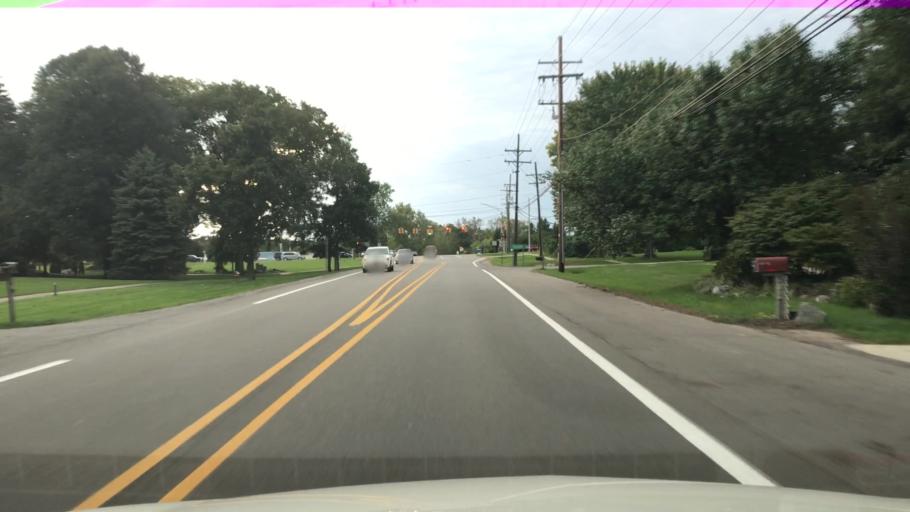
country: US
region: Michigan
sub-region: Oakland County
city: Rochester
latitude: 42.6826
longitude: -83.0919
